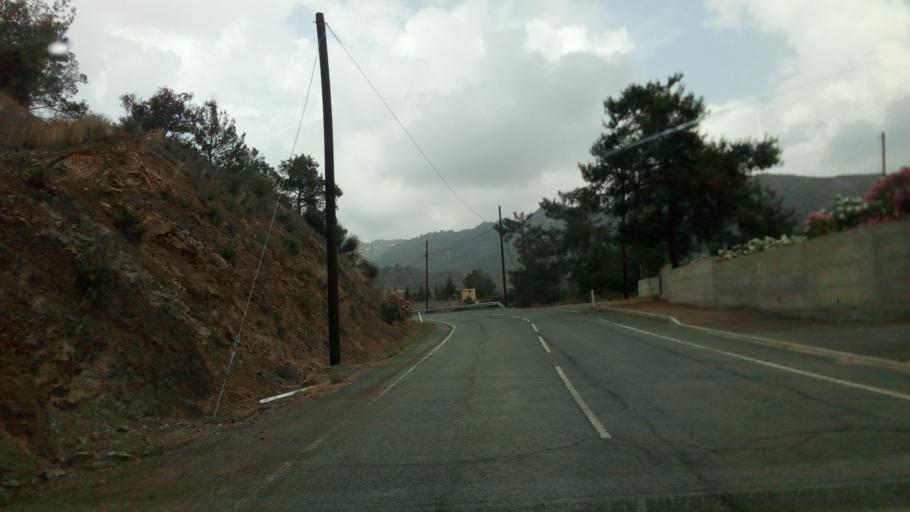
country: CY
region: Limassol
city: Parekklisha
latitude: 34.8652
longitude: 33.1873
